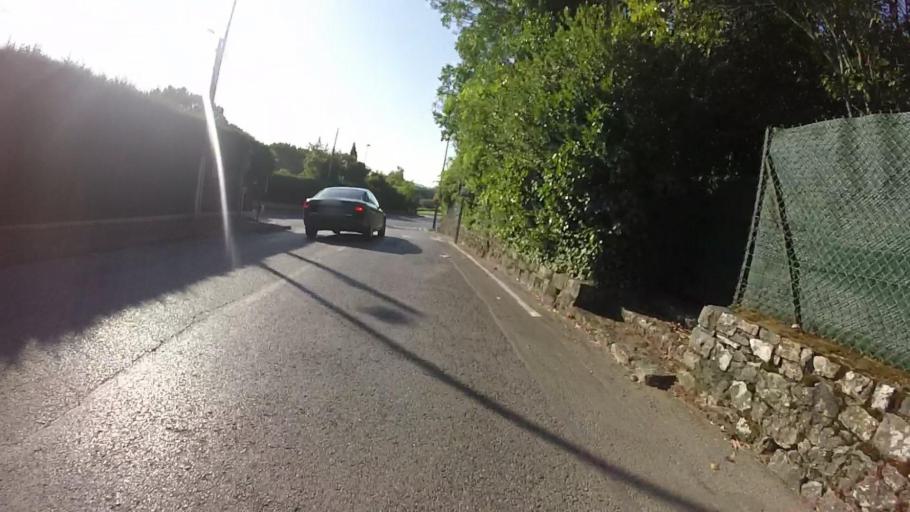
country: FR
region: Provence-Alpes-Cote d'Azur
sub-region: Departement des Alpes-Maritimes
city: Mougins
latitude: 43.6092
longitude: 7.0088
